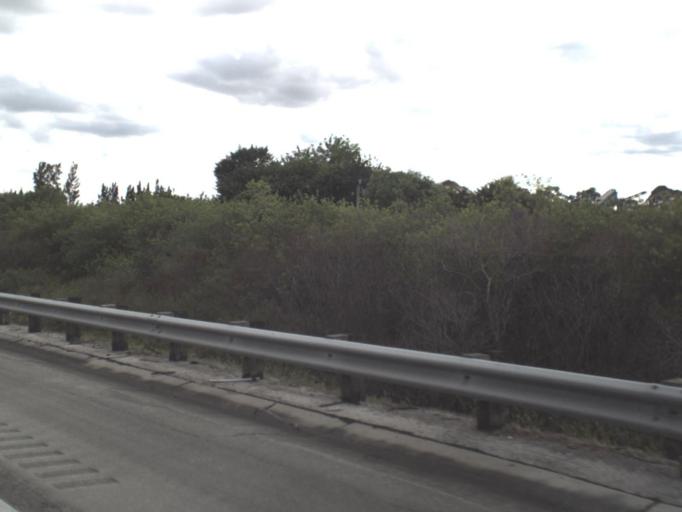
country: US
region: Florida
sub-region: Saint Lucie County
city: Fort Pierce South
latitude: 27.3769
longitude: -80.3853
